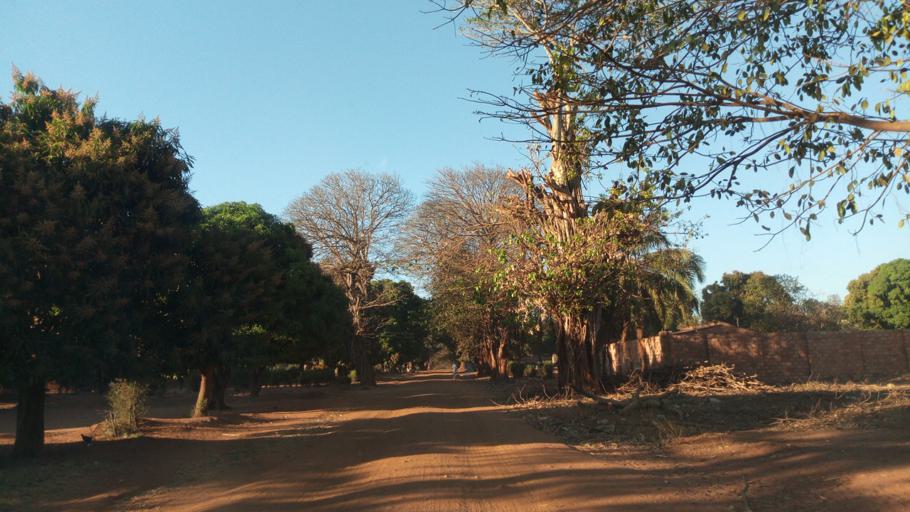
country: ZM
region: Luapula
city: Mwense
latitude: -10.3864
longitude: 28.6162
